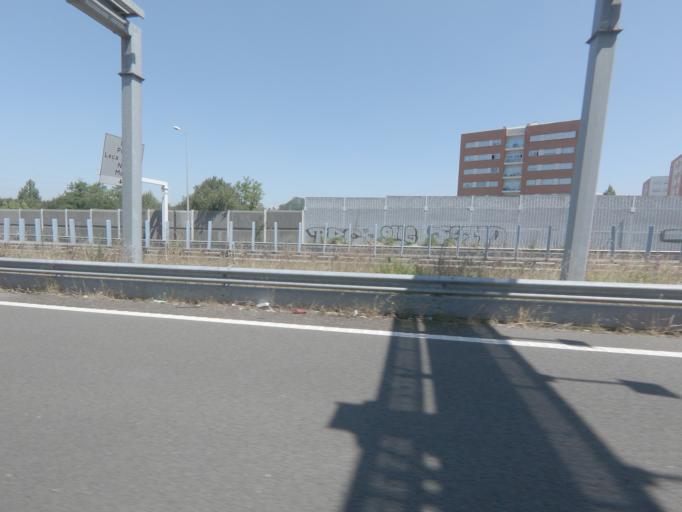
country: PT
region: Porto
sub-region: Maia
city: Leca do Bailio
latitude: 41.2024
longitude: -8.6176
